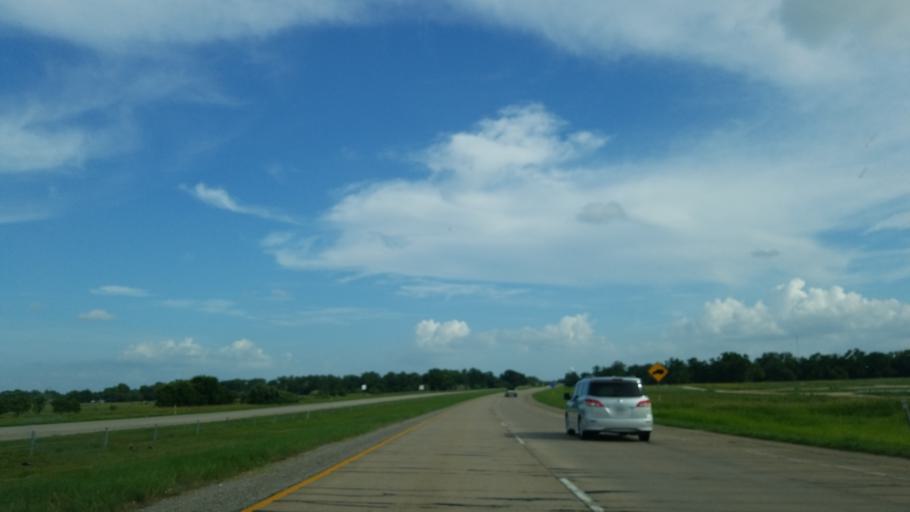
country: US
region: Texas
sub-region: Colorado County
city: Columbus
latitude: 29.7281
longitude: -96.5811
